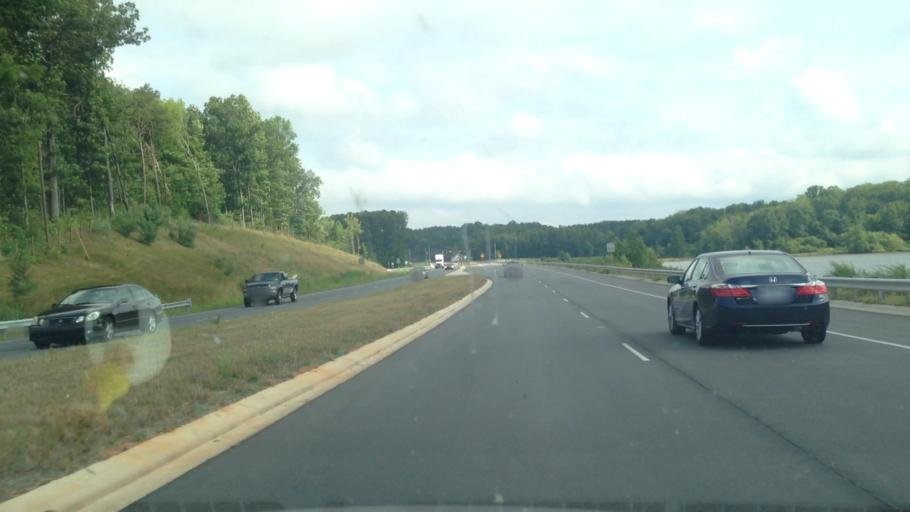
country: US
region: North Carolina
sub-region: Guilford County
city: Summerfield
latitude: 36.1706
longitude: -79.8799
